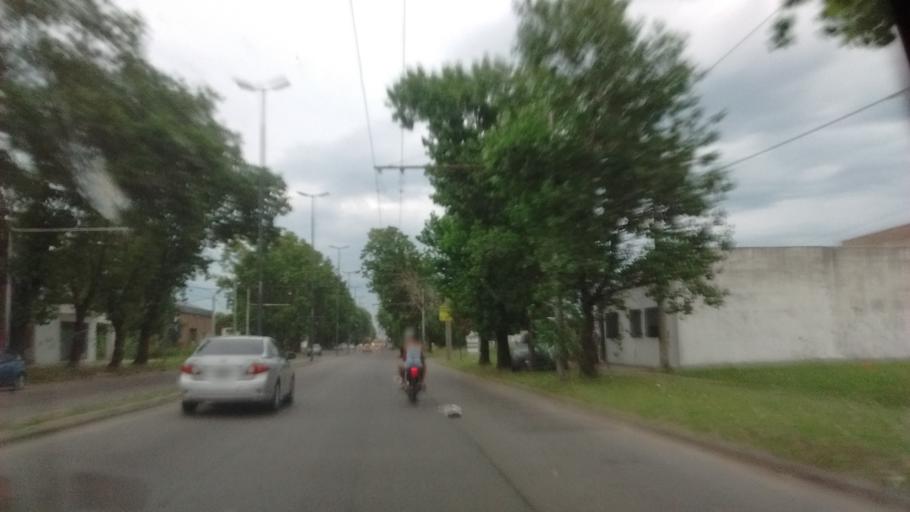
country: AR
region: Santa Fe
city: Perez
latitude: -32.9401
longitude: -60.7345
